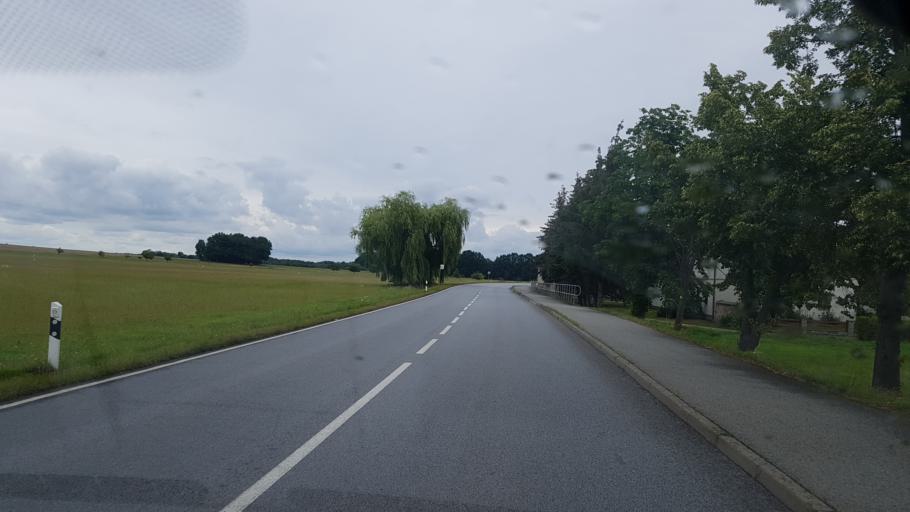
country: DE
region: Saxony
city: Quitzdorf
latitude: 51.2216
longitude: 14.7793
